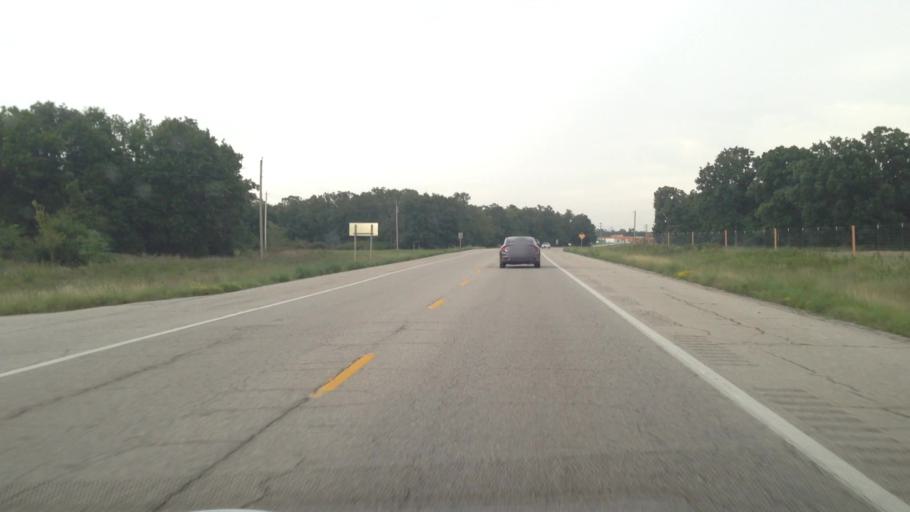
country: US
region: Kansas
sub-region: Cherokee County
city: Galena
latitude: 37.0077
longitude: -94.6215
